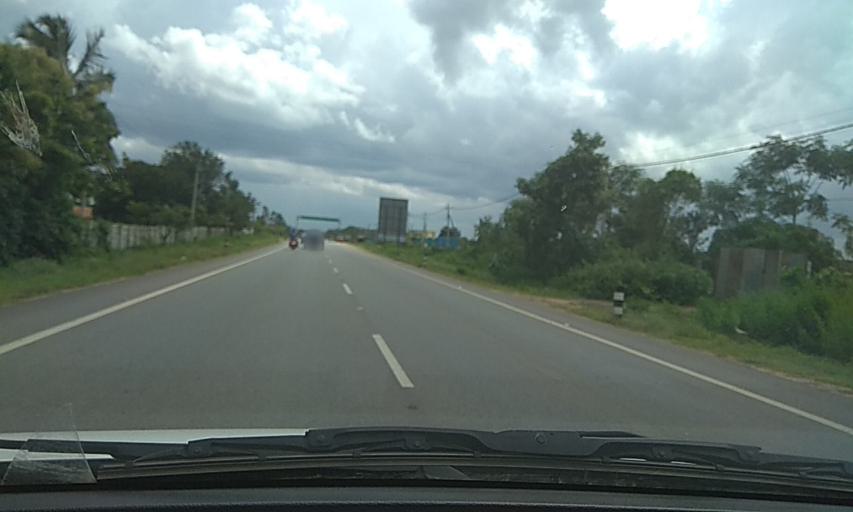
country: IN
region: Karnataka
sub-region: Tumkur
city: Tumkur
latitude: 13.2353
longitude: 77.0731
